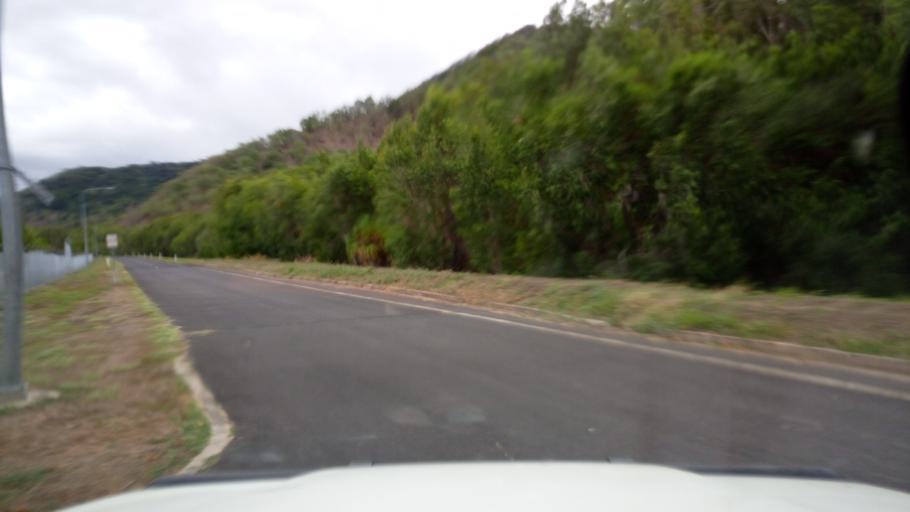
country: AU
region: Queensland
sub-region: Cairns
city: Redlynch
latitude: -16.8737
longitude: 145.7443
